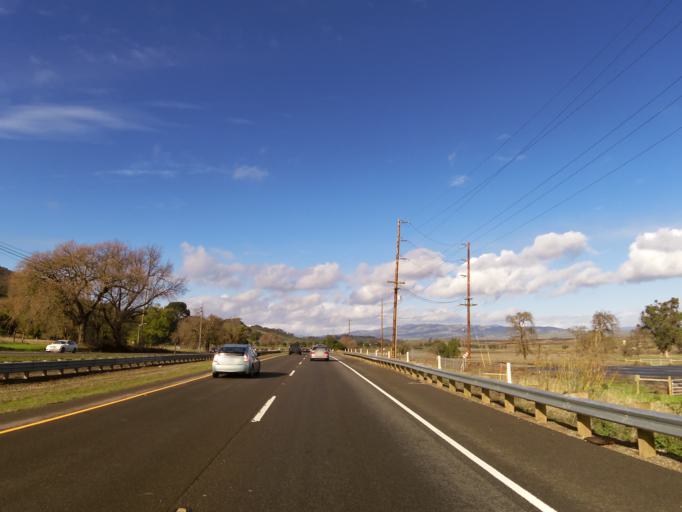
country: US
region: California
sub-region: Marin County
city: Novato
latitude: 38.1551
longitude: -122.5679
